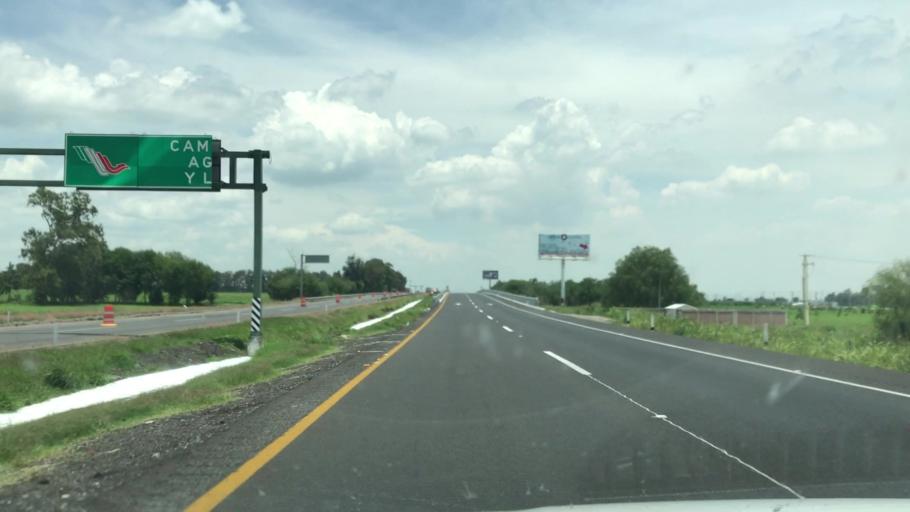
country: MX
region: Guanajuato
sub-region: Irapuato
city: Cuarta Brigada
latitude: 20.6512
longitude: -101.2840
